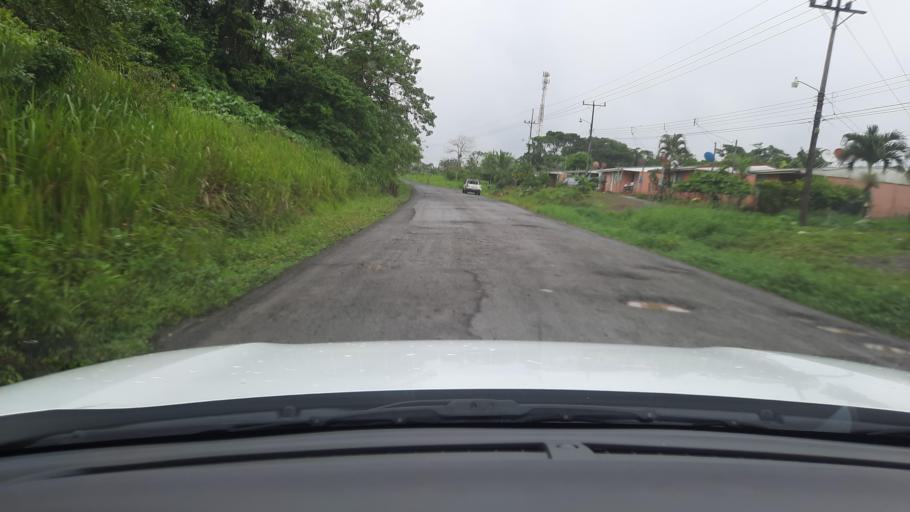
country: CR
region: Alajuela
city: San Jose
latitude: 11.0102
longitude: -85.3463
